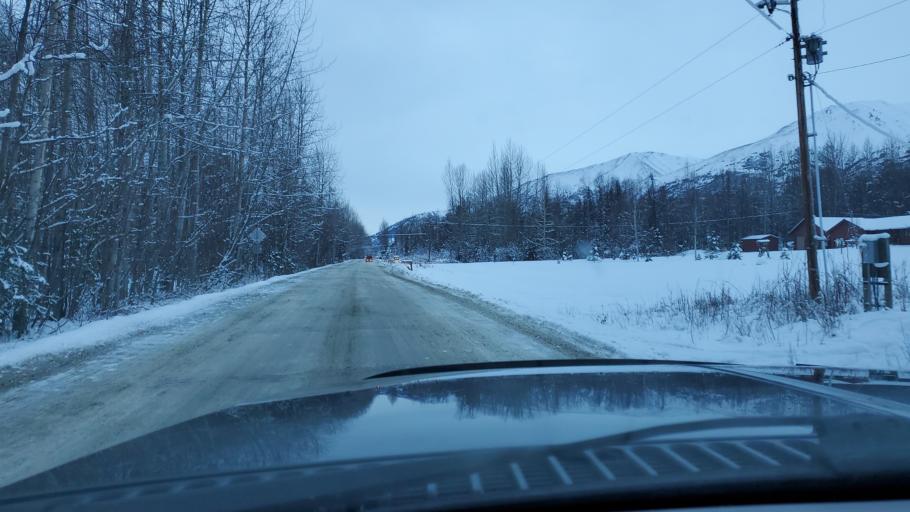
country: US
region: Alaska
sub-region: Matanuska-Susitna Borough
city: Fishhook
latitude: 61.6933
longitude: -149.3003
